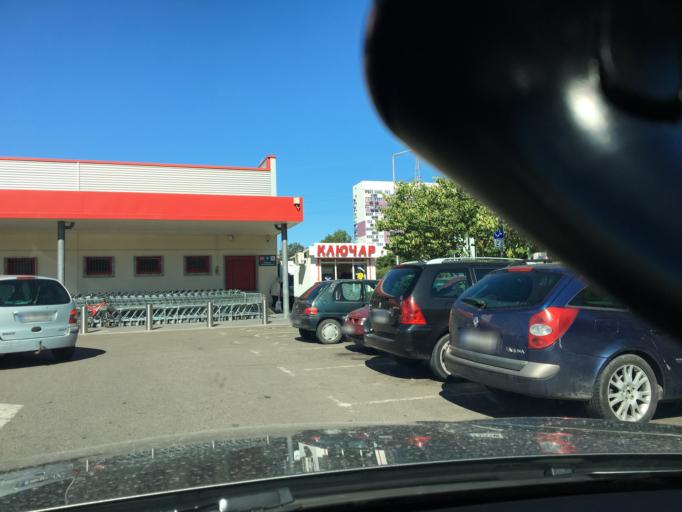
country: BG
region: Burgas
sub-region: Obshtina Burgas
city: Burgas
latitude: 42.5151
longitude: 27.4510
